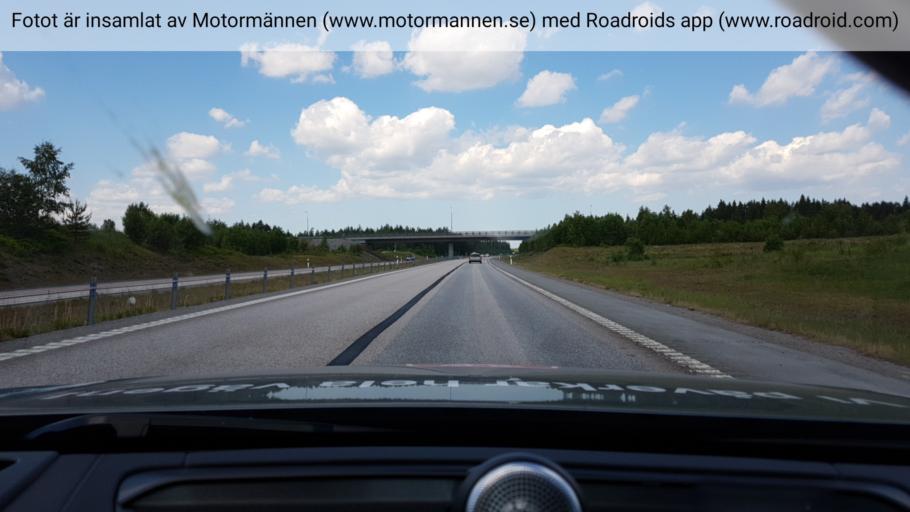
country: SE
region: Uppsala
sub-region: Tierps Kommun
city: Tierp
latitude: 60.2135
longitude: 17.4957
